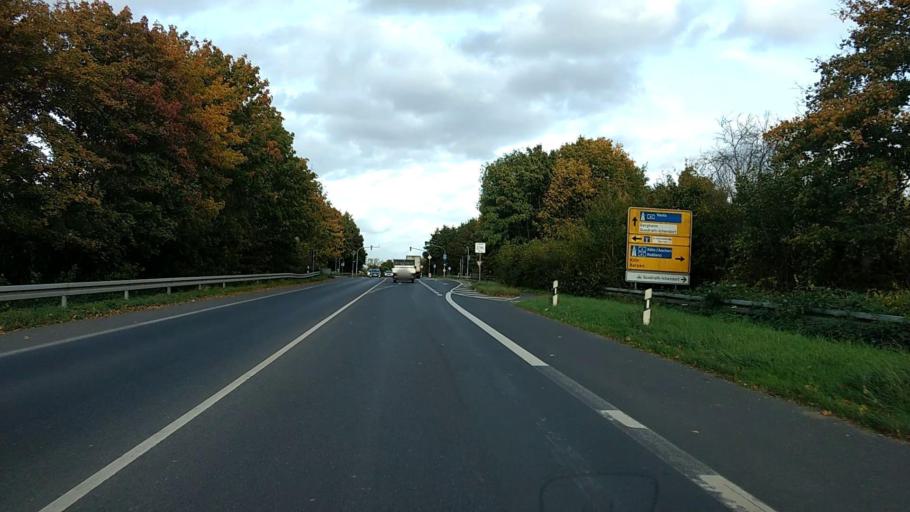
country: DE
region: North Rhine-Westphalia
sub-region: Regierungsbezirk Koln
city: Bergheim
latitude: 50.9356
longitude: 6.6470
